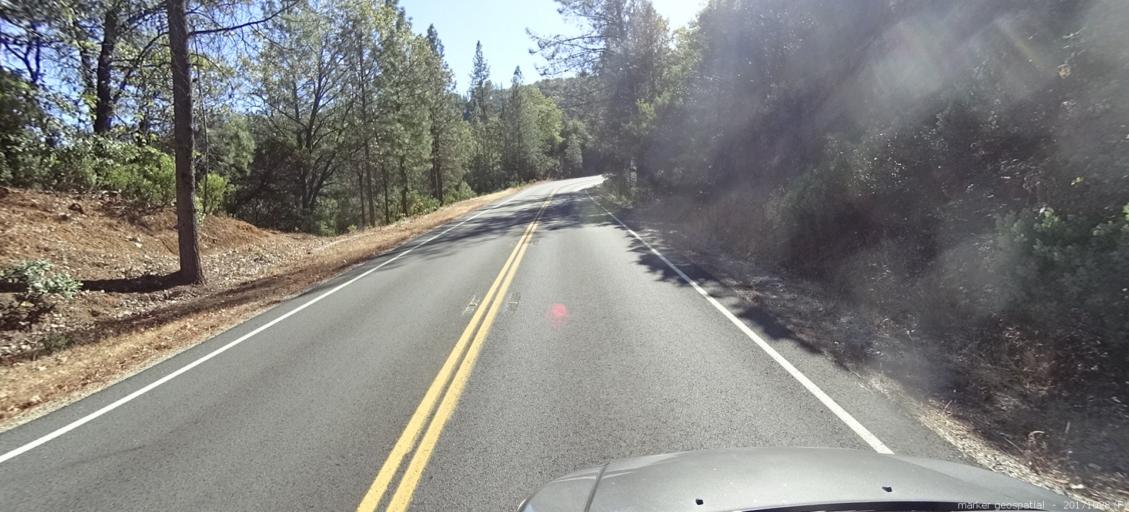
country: US
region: California
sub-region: Shasta County
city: Shasta
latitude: 40.6145
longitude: -122.5653
